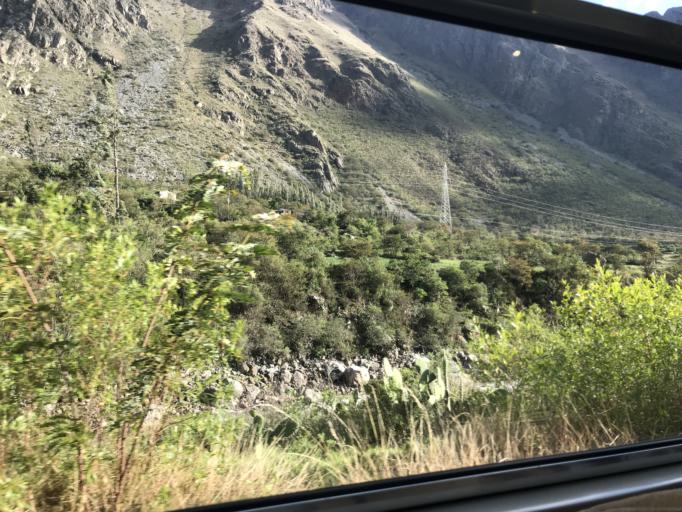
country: PE
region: Cusco
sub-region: Provincia de Urubamba
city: Ollantaytambo
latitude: -13.2271
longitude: -72.4036
